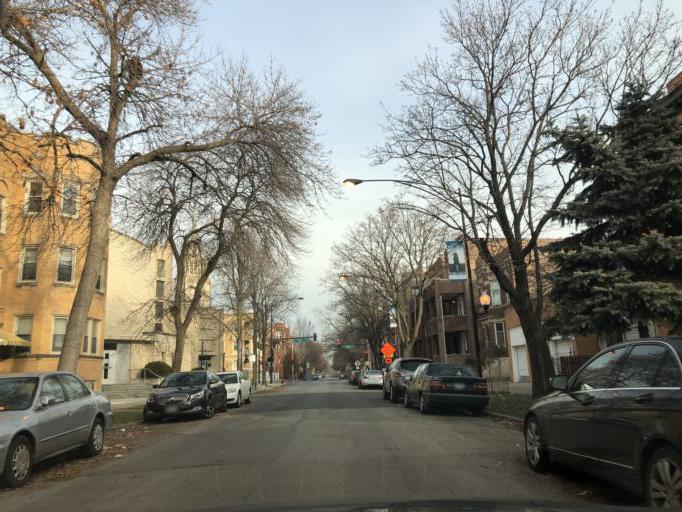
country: US
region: Illinois
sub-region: Cook County
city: Chicago
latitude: 41.8986
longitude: -87.6845
